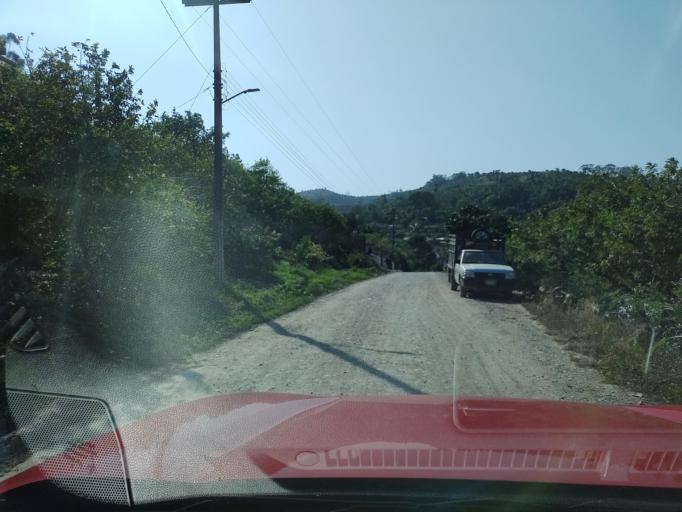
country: MX
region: Veracruz
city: Agua Dulce
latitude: 20.2903
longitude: -97.1830
